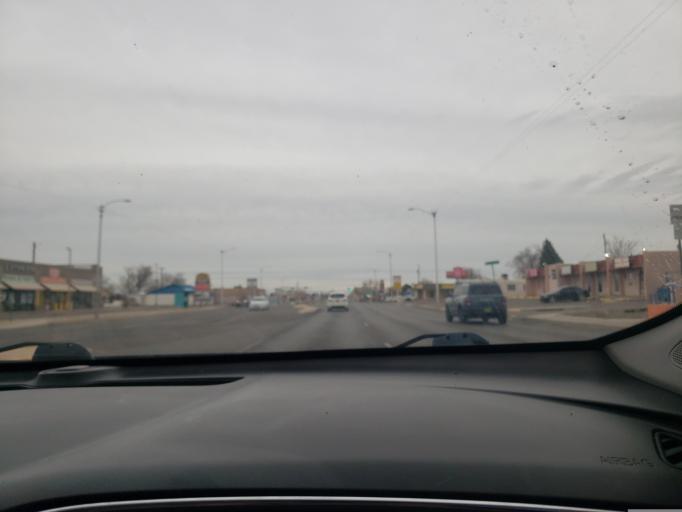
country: US
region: New Mexico
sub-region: Bernalillo County
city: North Valley
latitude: 35.1215
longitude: -106.5864
